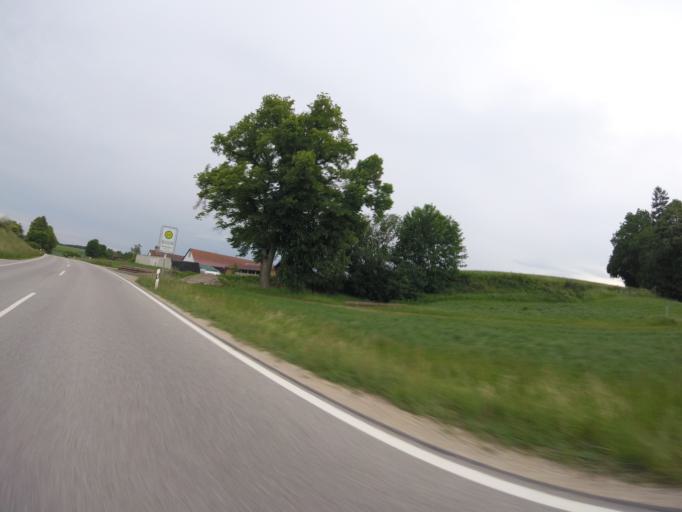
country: DE
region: Bavaria
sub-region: Upper Bavaria
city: Hohenkammer
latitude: 48.3936
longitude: 11.5381
